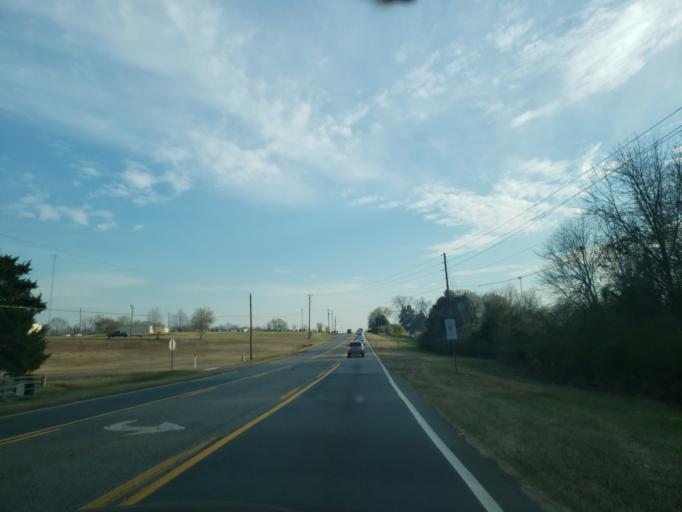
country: US
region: Alabama
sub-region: Hale County
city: Moundville
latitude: 32.9941
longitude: -87.6242
